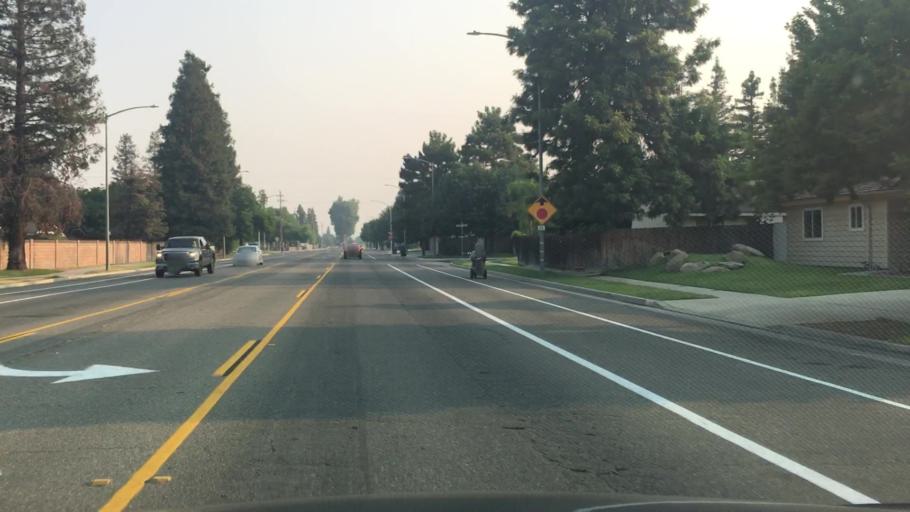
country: US
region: California
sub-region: Fresno County
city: Clovis
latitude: 36.8288
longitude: -119.6729
